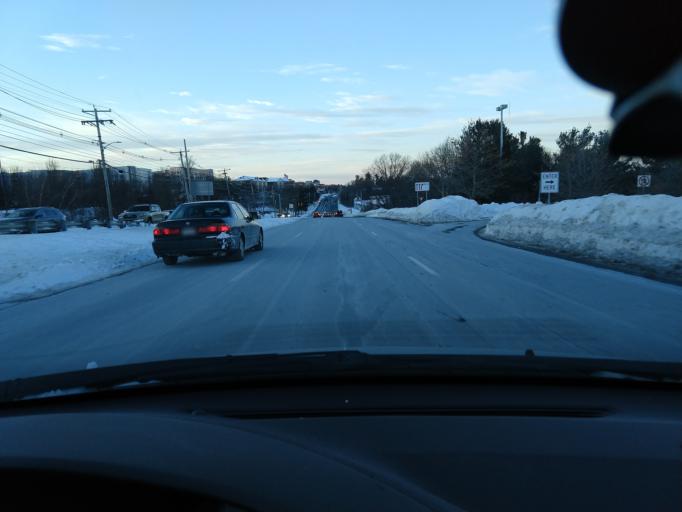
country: US
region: Massachusetts
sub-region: Middlesex County
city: Burlington
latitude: 42.4828
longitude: -71.2184
